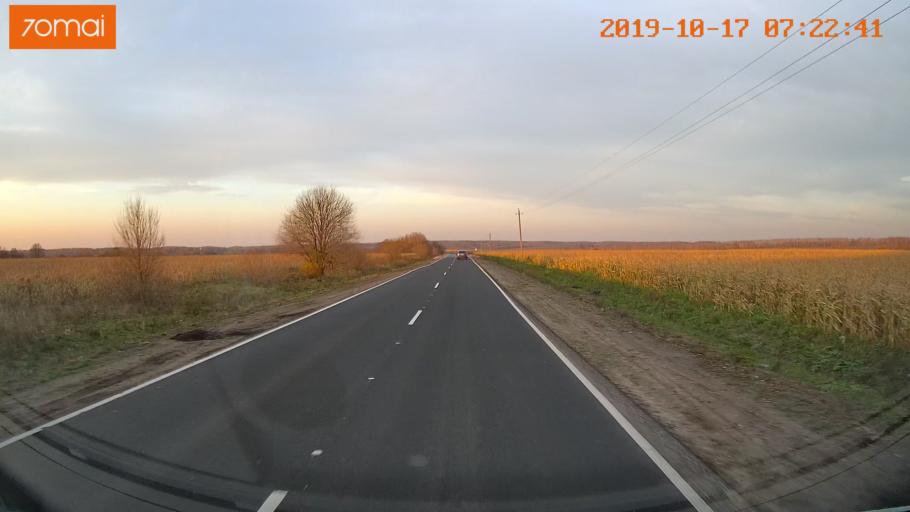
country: RU
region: Ivanovo
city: Gavrilov Posad
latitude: 56.3413
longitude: 40.1351
